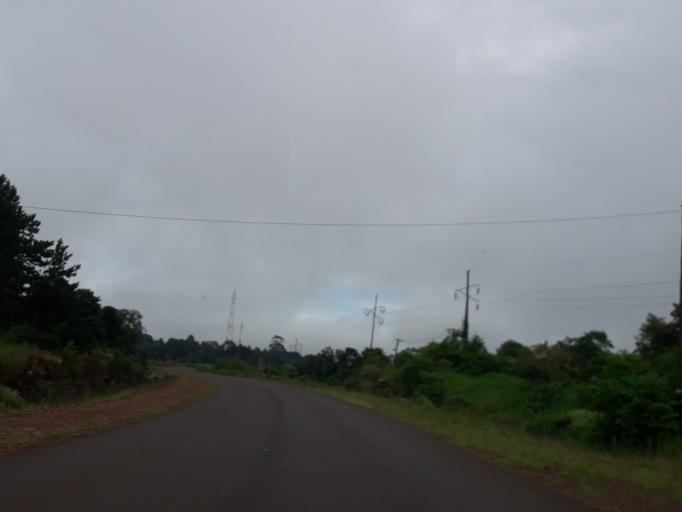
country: AR
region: Misiones
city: Bernardo de Irigoyen
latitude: -26.4219
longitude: -53.8381
